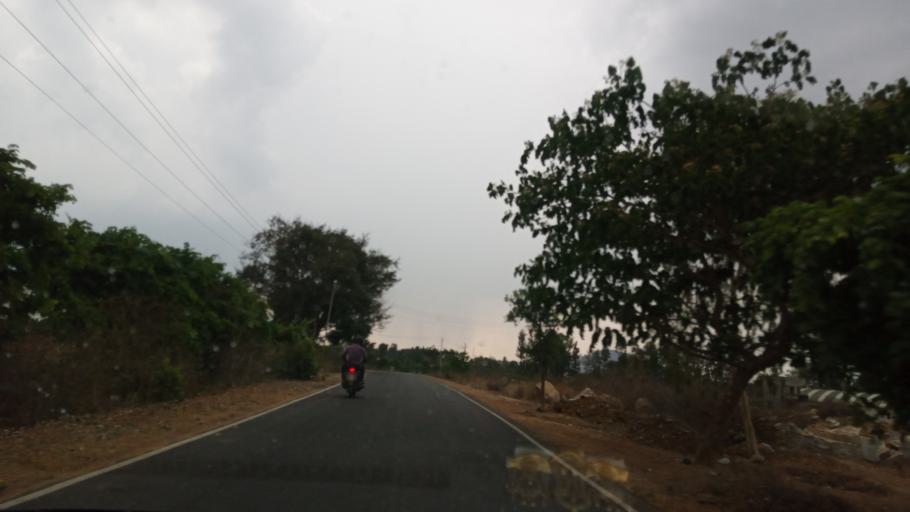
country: IN
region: Karnataka
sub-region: Kolar
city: Mulbagal
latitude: 13.1317
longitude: 78.3556
